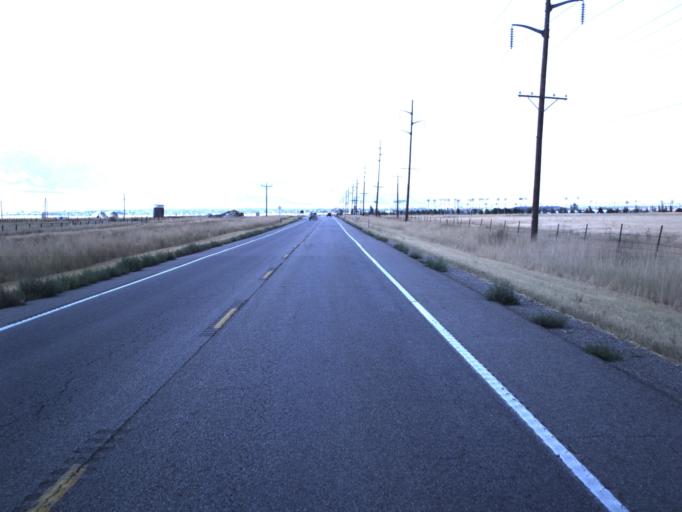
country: US
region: Utah
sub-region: Tooele County
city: Tooele
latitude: 40.5638
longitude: -112.3603
